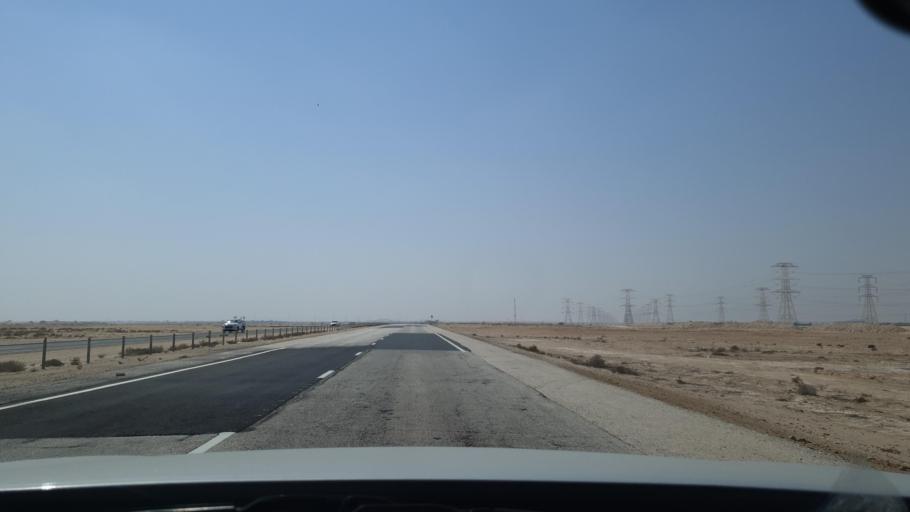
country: QA
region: Al Khawr
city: Al Khawr
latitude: 25.7050
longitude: 51.4450
